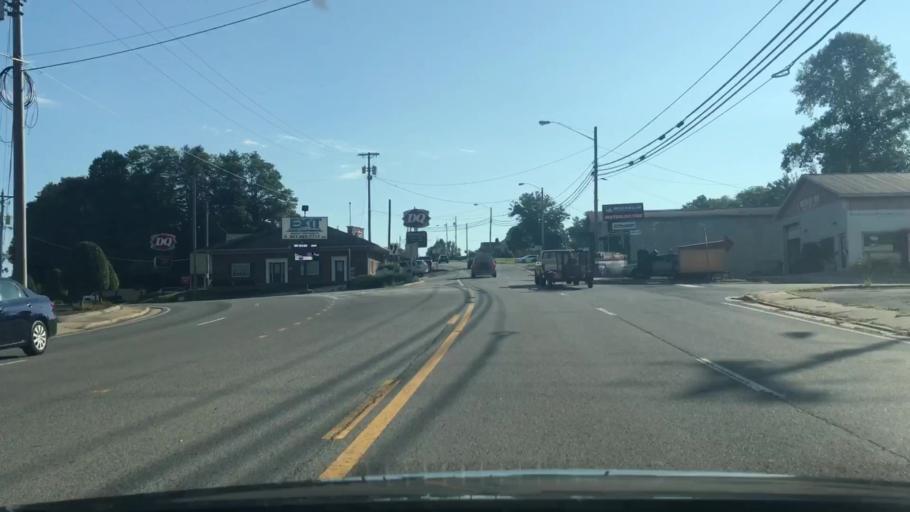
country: US
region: Tennessee
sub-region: Overton County
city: Livingston
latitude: 36.3804
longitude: -85.3299
